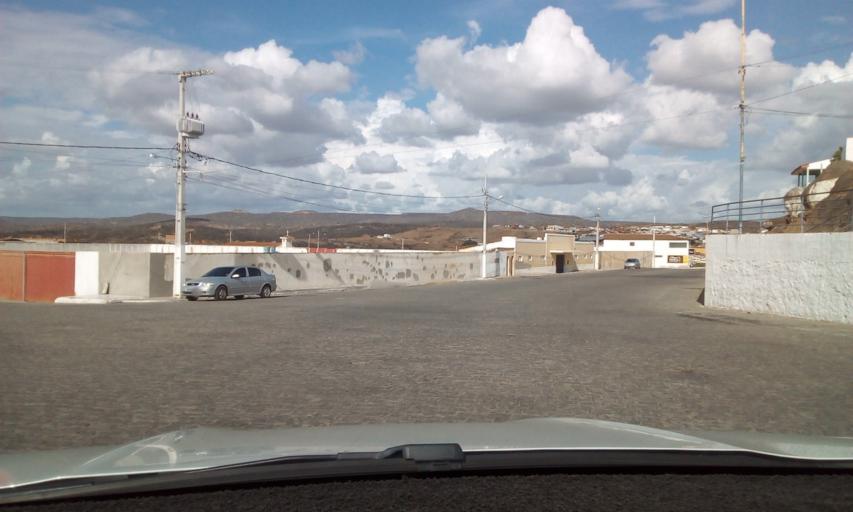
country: BR
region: Paraiba
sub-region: Picui
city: Picui
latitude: -6.5087
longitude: -36.3496
